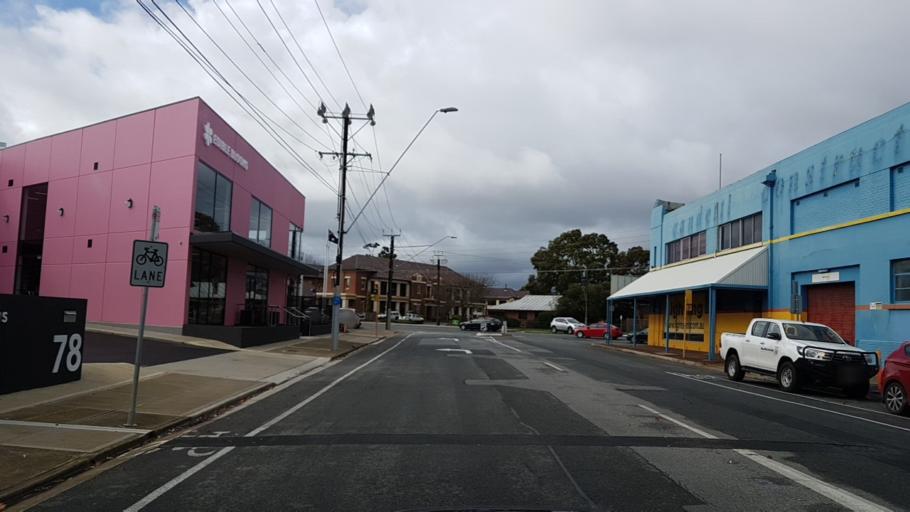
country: AU
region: South Australia
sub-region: Unley
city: Forestville
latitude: -34.9459
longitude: 138.5787
